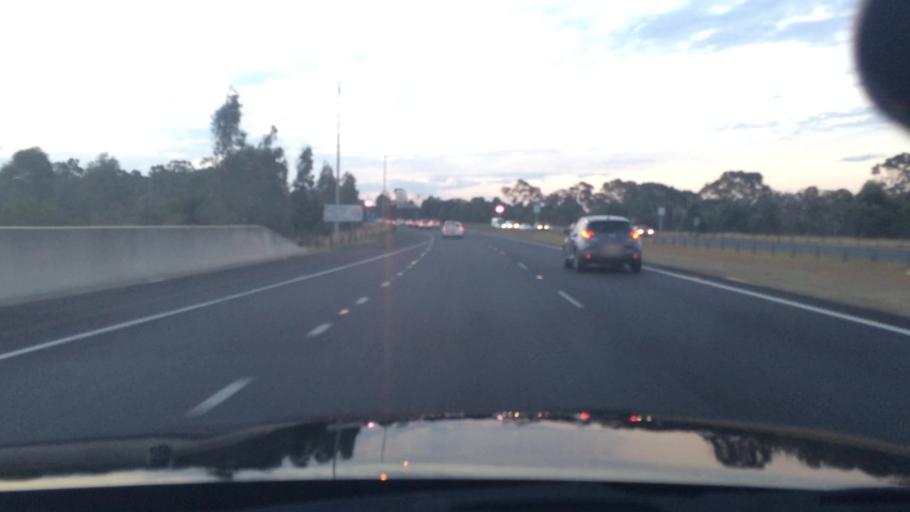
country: AU
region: New South Wales
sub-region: Blacktown
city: Doonside
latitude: -33.7837
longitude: 150.8580
